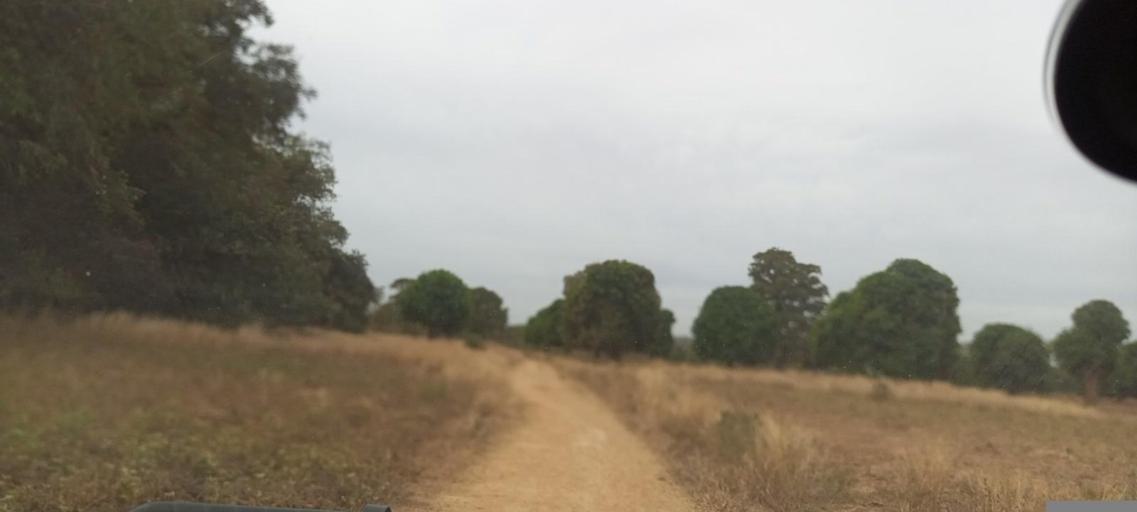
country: ML
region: Koulikoro
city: Kati
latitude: 12.7703
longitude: -8.3709
